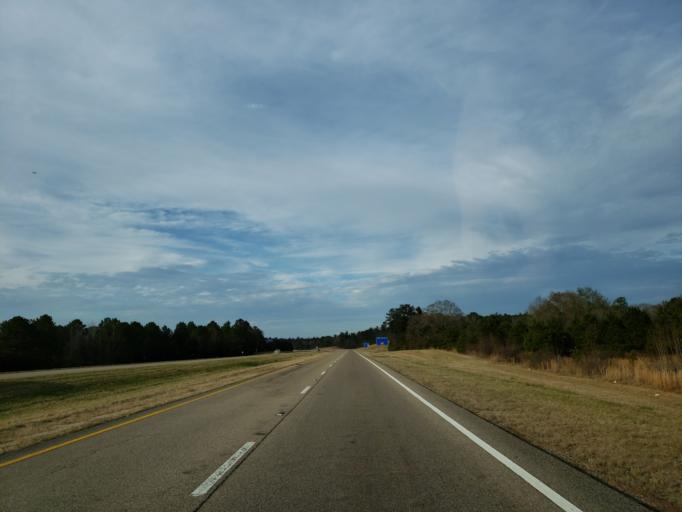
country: US
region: Mississippi
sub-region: Wayne County
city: Waynesboro
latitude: 31.6896
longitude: -88.6173
